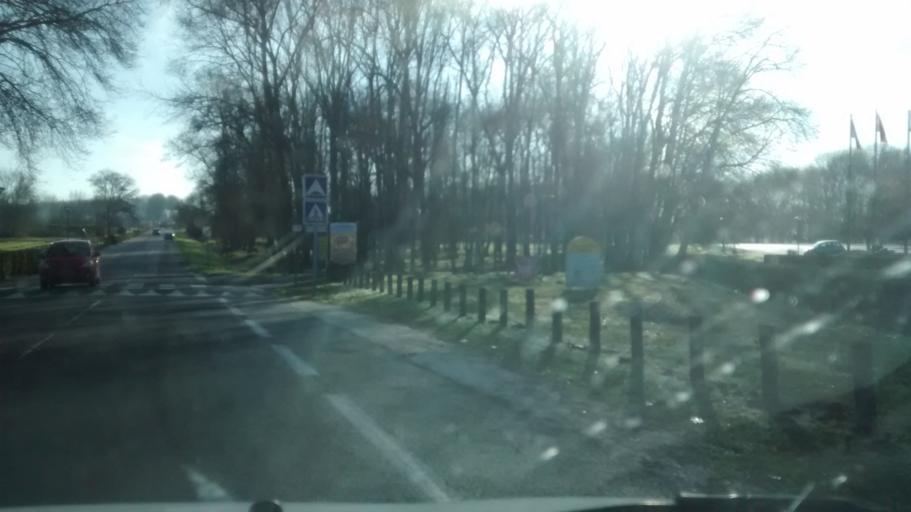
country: FR
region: Centre
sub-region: Departement d'Indre-et-Loire
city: Nazelles-Negron
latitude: 47.4305
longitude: 0.9551
